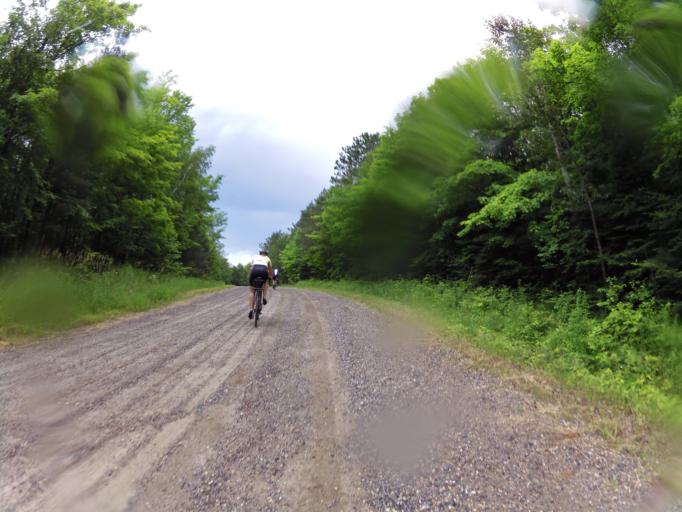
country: CA
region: Ontario
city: Renfrew
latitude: 45.1057
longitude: -76.6132
